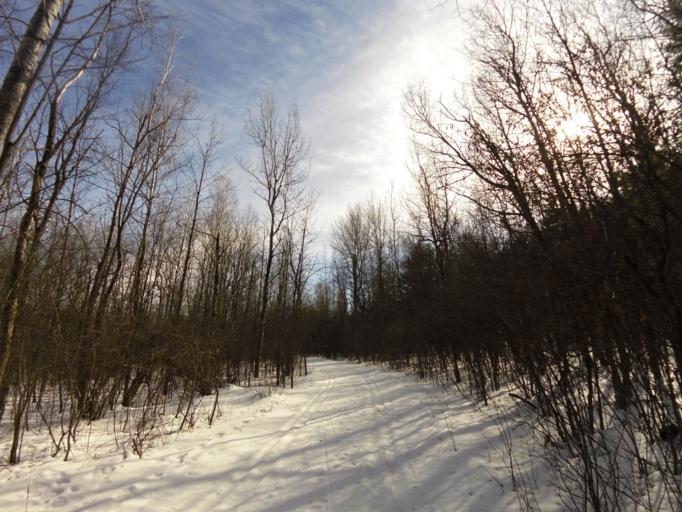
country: CA
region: Quebec
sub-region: Outaouais
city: Gatineau
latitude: 45.4567
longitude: -75.7728
